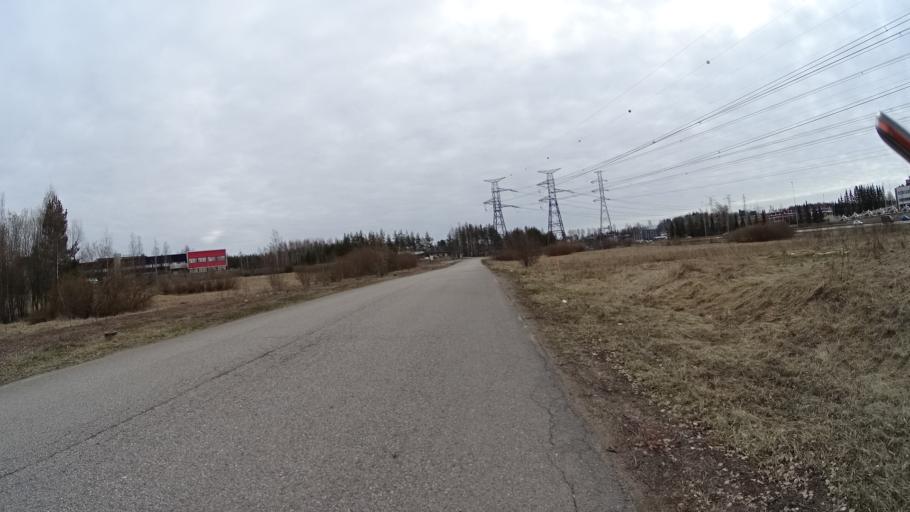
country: FI
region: Uusimaa
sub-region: Helsinki
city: Teekkarikylae
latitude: 60.2994
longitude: 24.8894
